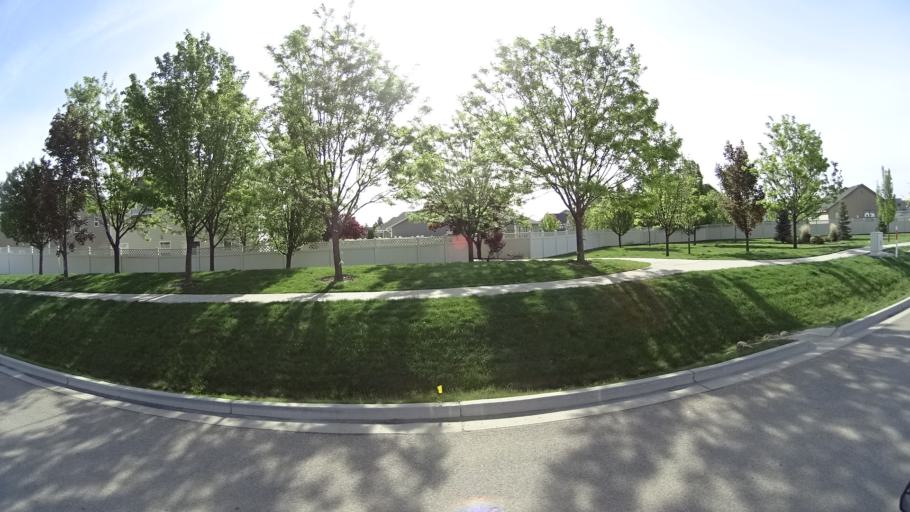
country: US
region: Idaho
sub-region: Ada County
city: Kuna
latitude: 43.5150
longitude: -116.4039
